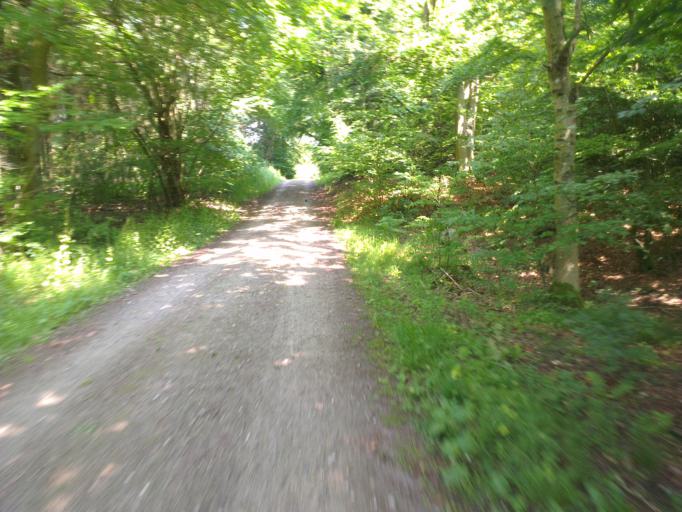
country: DK
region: Capital Region
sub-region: Allerod Kommune
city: Lillerod
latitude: 55.9212
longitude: 12.3608
